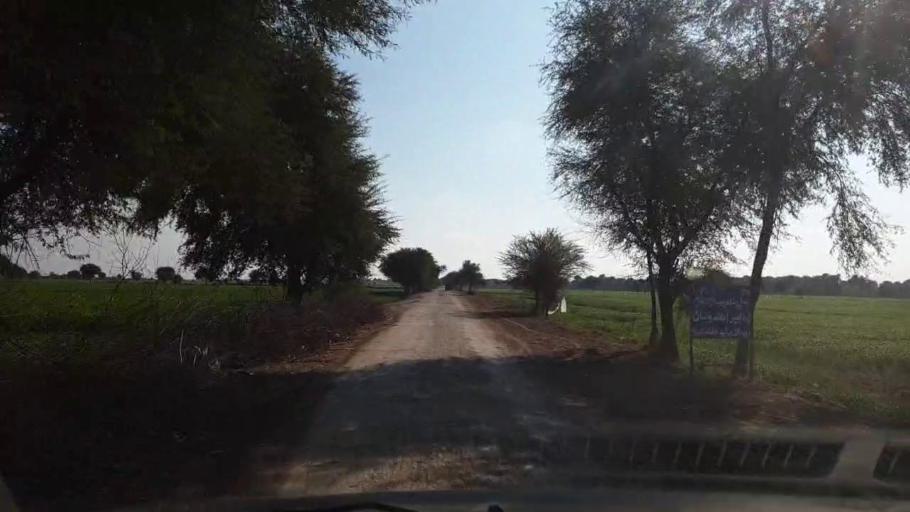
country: PK
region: Sindh
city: Sinjhoro
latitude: 25.9853
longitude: 68.7261
